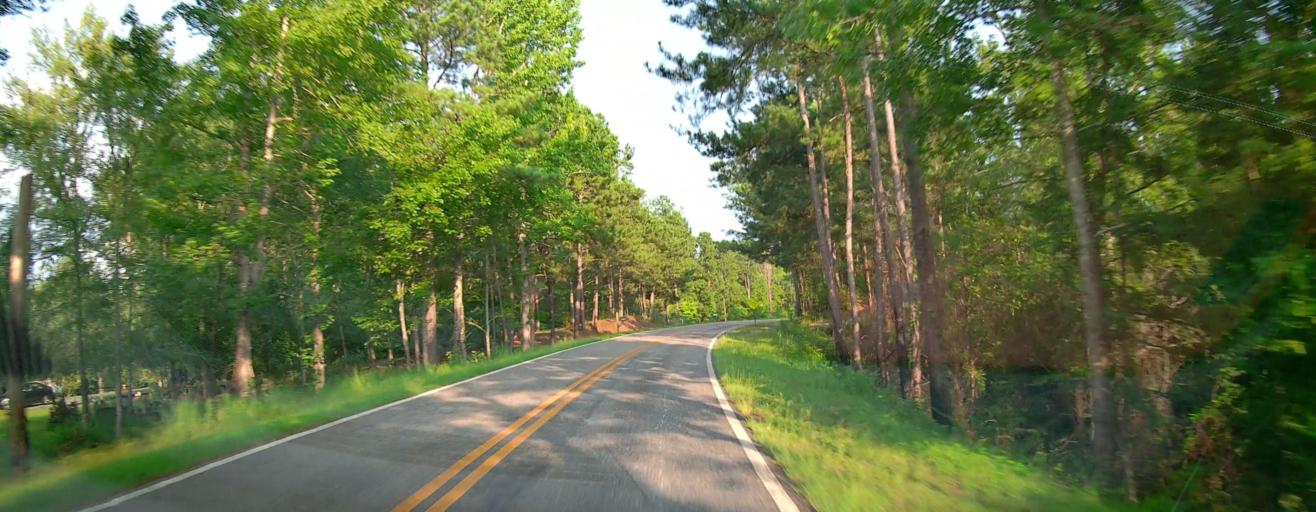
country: US
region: Georgia
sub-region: Monroe County
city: Forsyth
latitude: 33.0957
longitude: -83.7549
